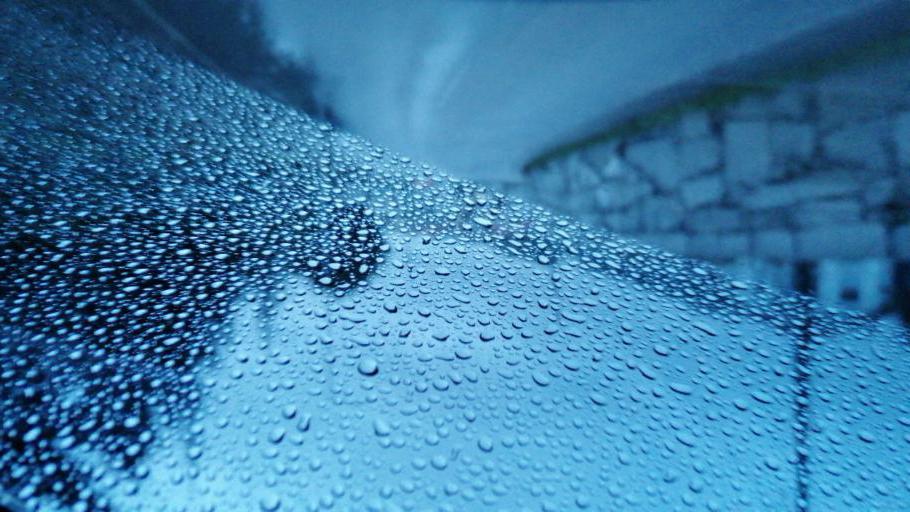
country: PT
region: Vila Real
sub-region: Vila Pouca de Aguiar
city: Vila Pouca de Aguiar
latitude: 41.4926
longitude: -7.6457
